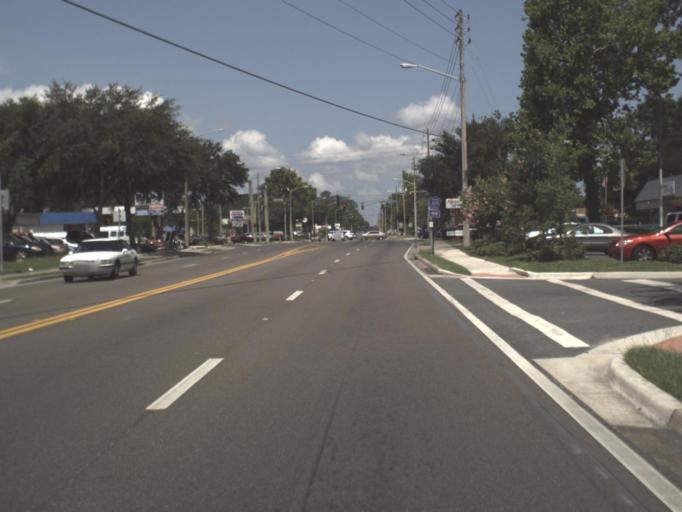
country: US
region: Florida
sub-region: Alachua County
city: Gainesville
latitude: 29.6739
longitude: -82.3199
